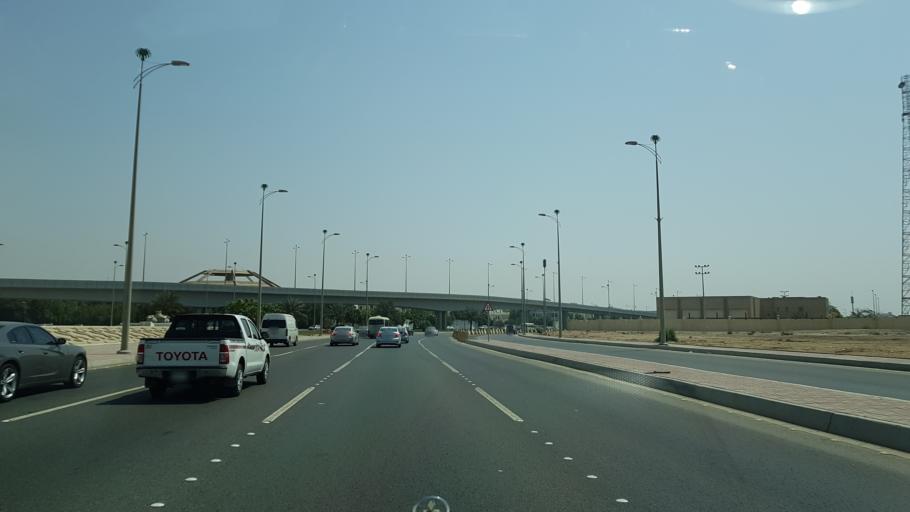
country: SA
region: Makkah
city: Jeddah
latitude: 21.5417
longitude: 39.1535
